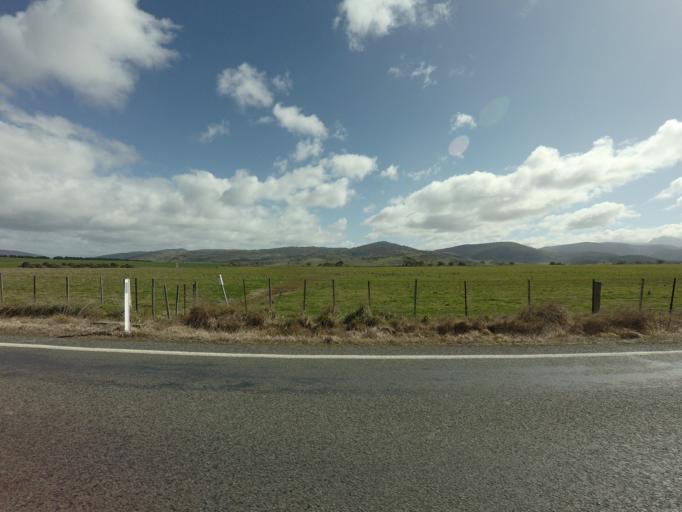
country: AU
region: Tasmania
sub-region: Northern Midlands
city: Evandale
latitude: -41.7960
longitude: 147.7073
